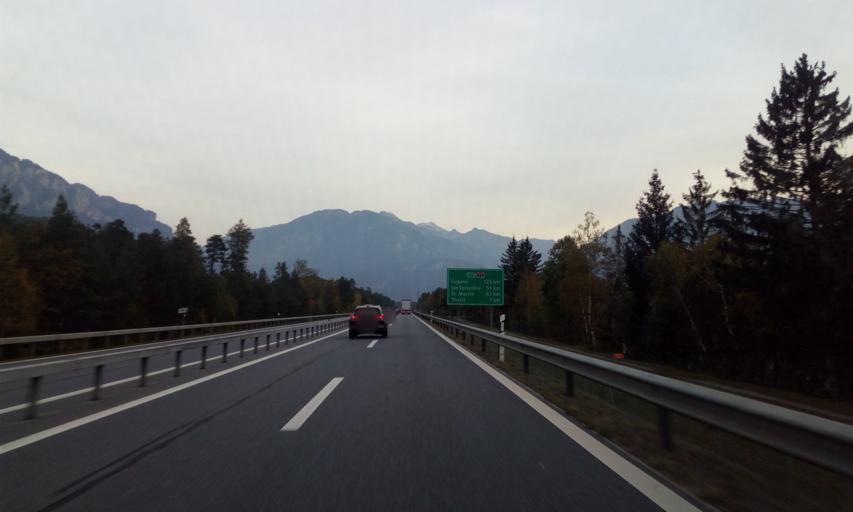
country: CH
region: Grisons
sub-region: Hinterrhein District
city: Cazis
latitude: 46.7550
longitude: 9.4266
